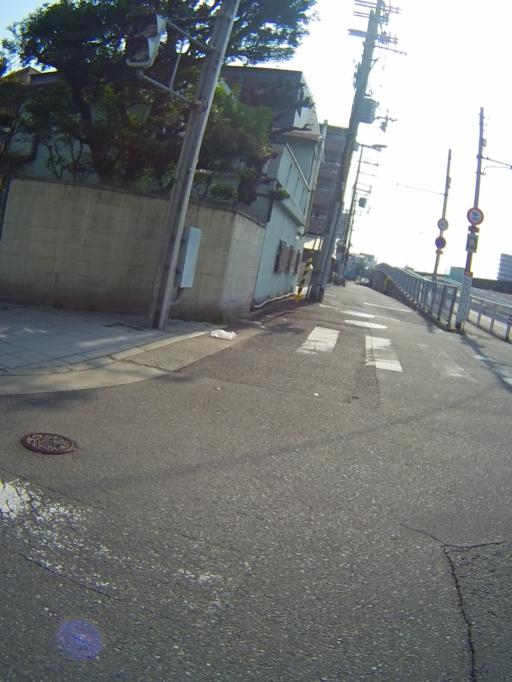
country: JP
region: Hyogo
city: Amagasaki
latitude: 34.6852
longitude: 135.4523
